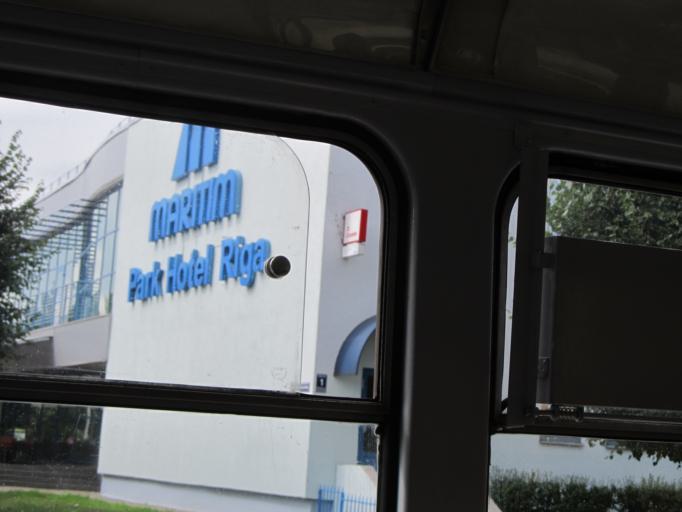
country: LV
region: Riga
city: Riga
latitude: 56.9420
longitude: 24.0823
